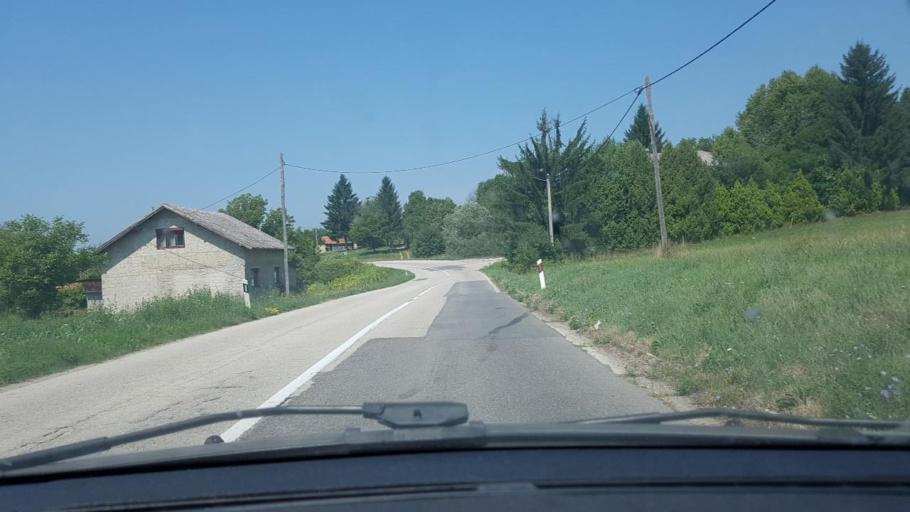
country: BA
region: Federation of Bosnia and Herzegovina
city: Velika Kladusa
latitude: 45.2166
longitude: 15.7549
